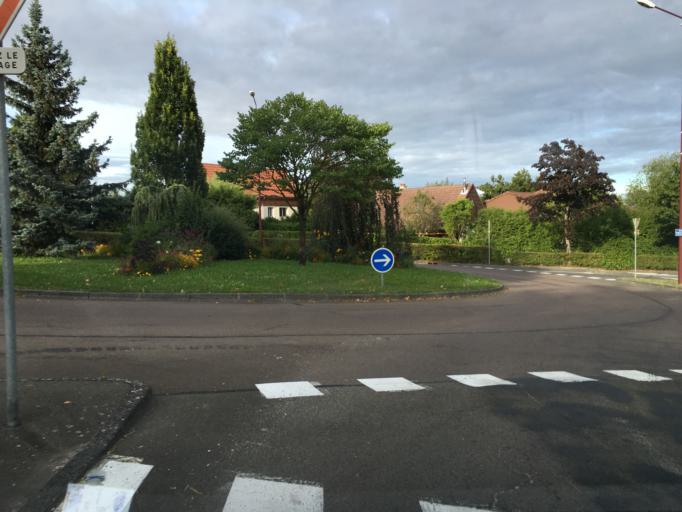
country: FR
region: Bourgogne
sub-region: Departement de la Cote-d'Or
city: Talant
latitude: 47.3392
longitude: 4.9974
